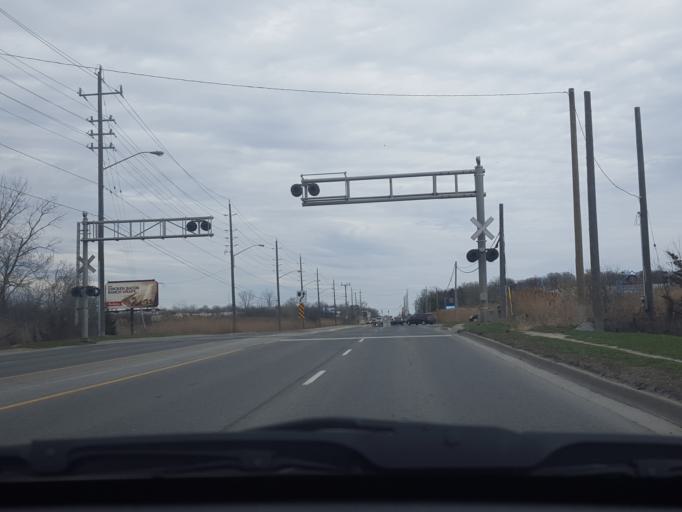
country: CA
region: Ontario
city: Ajax
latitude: 43.8340
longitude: -79.0633
